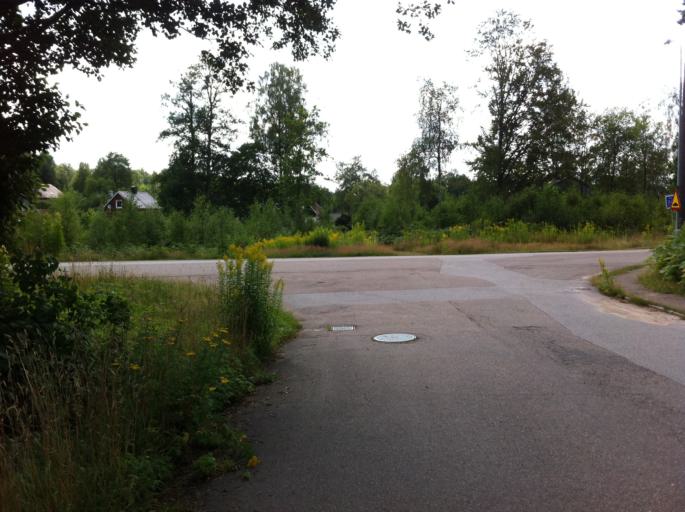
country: SE
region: Halland
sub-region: Hylte Kommun
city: Hyltebruk
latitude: 56.9977
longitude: 13.2414
